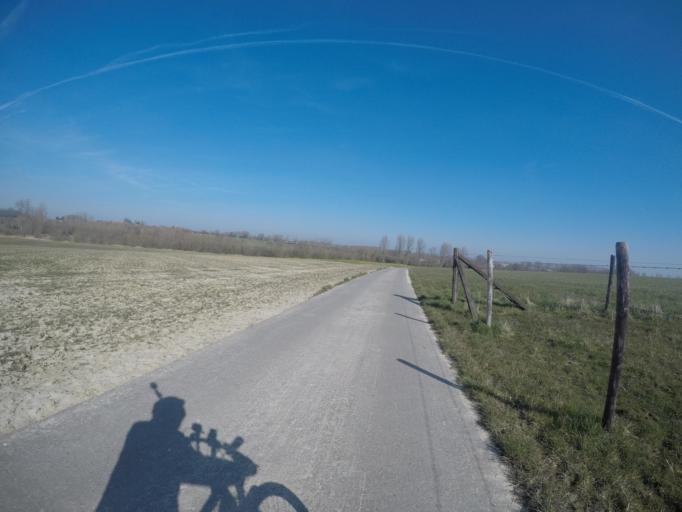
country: BE
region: Flanders
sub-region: Provincie Oost-Vlaanderen
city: Sint-Maria-Lierde
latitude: 50.7994
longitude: 3.8647
